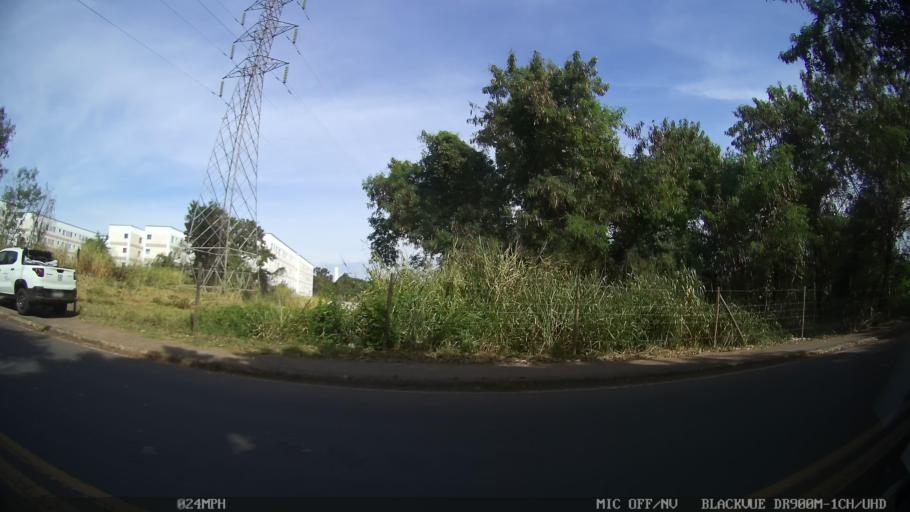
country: BR
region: Sao Paulo
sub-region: Piracicaba
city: Piracicaba
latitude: -22.7542
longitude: -47.6099
